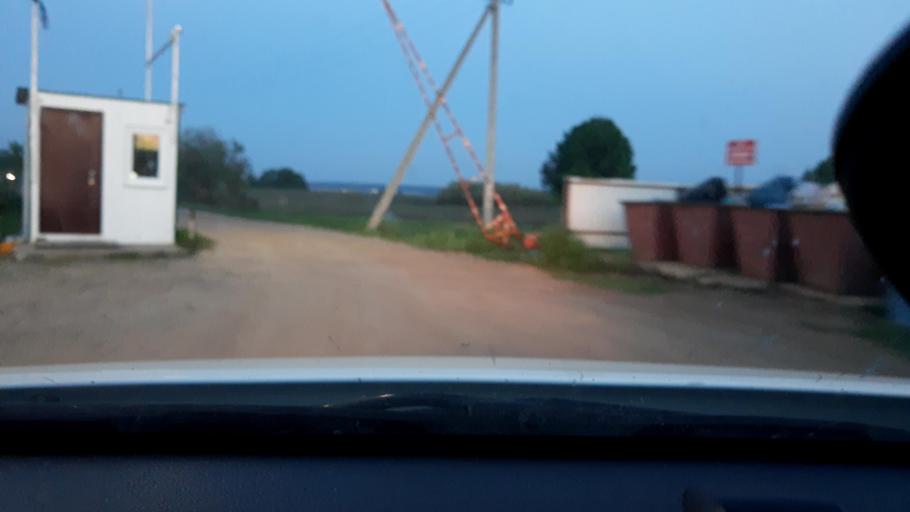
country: RU
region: Bashkortostan
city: Avdon
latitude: 54.5267
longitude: 55.8222
